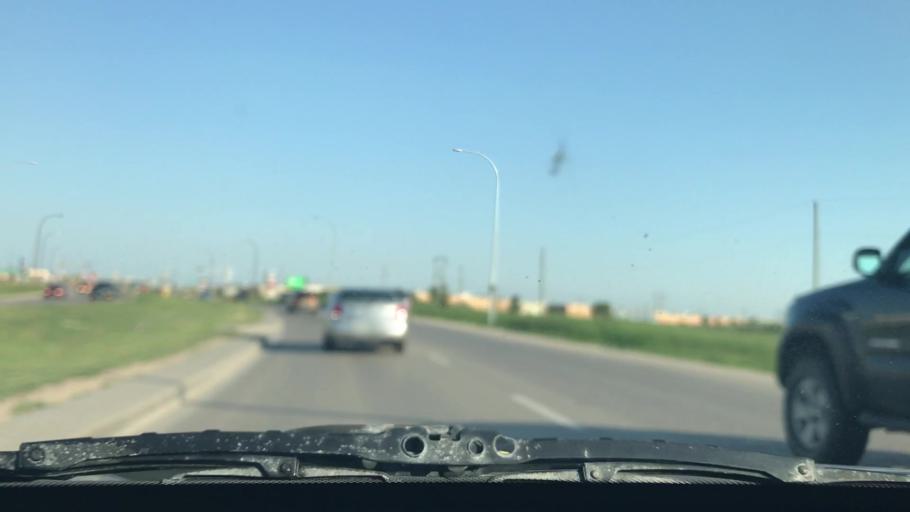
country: CA
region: Manitoba
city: Winnipeg
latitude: 49.8290
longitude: -97.2094
